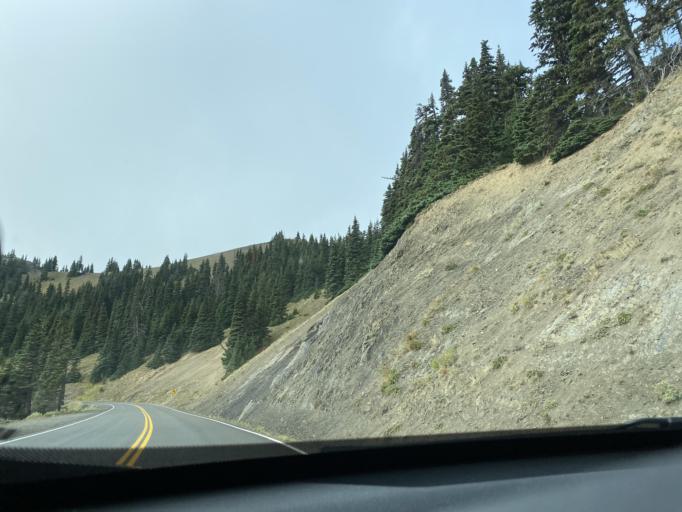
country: US
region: Washington
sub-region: Clallam County
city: Port Angeles
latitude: 47.9739
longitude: -123.4857
